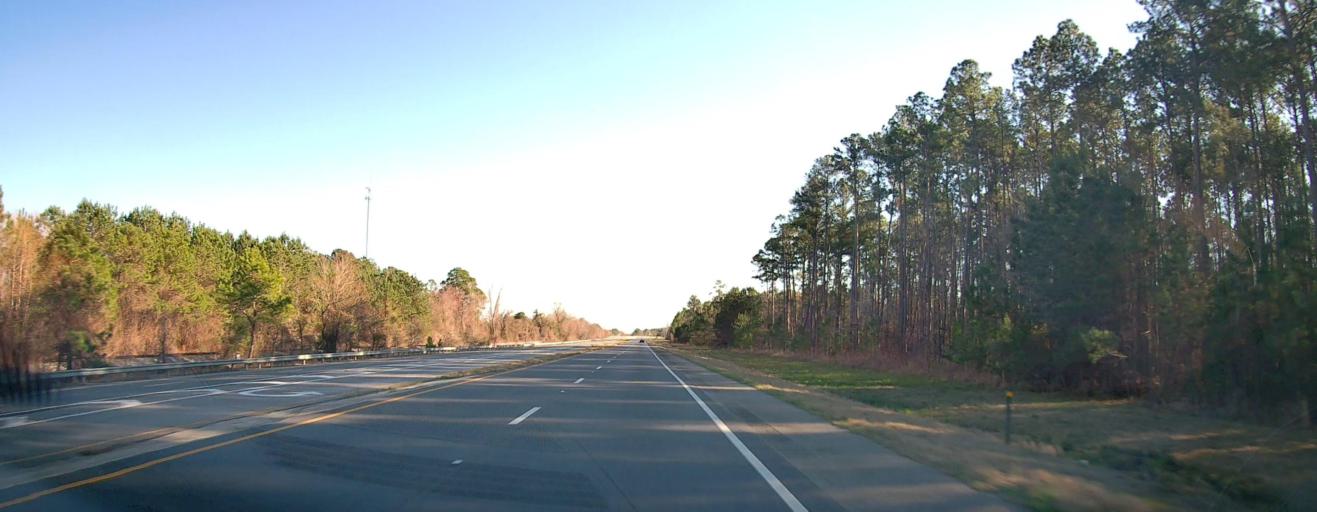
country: US
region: Georgia
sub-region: Lee County
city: Leesburg
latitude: 31.8313
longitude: -84.2193
